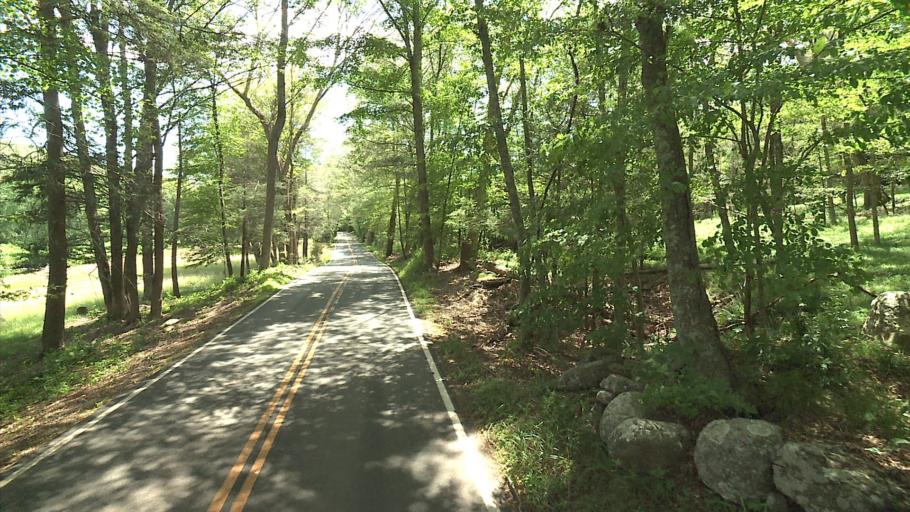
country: US
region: Connecticut
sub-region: New London County
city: Colchester
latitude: 41.4703
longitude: -72.3391
